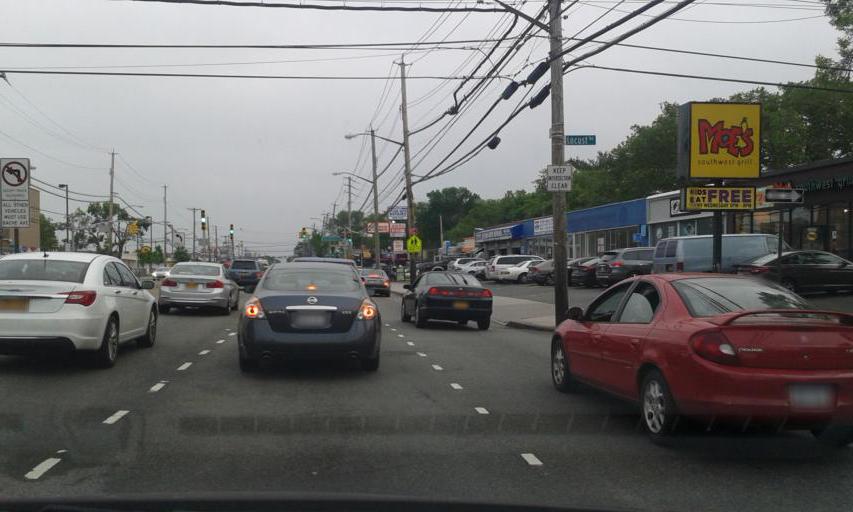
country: US
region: New York
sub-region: Richmond County
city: Staten Island
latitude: 40.5729
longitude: -74.1074
